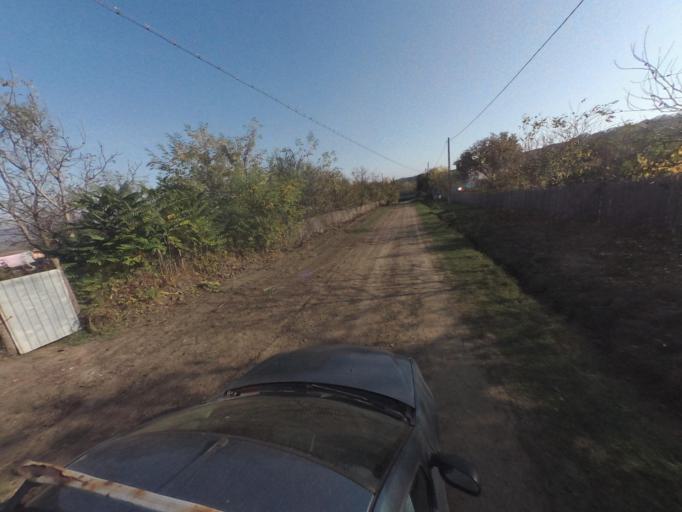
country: RO
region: Vaslui
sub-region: Comuna Bacesti
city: Bacesti
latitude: 46.8736
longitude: 27.1967
